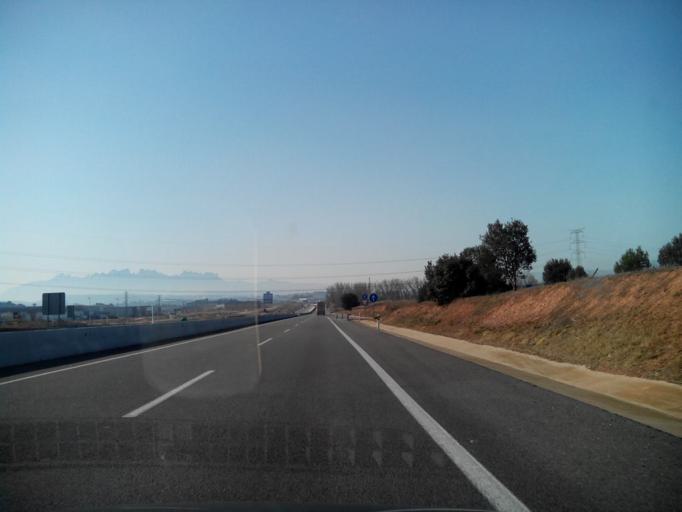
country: ES
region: Catalonia
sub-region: Provincia de Barcelona
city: Sant Fruitos de Bages
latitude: 41.7742
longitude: 1.8758
